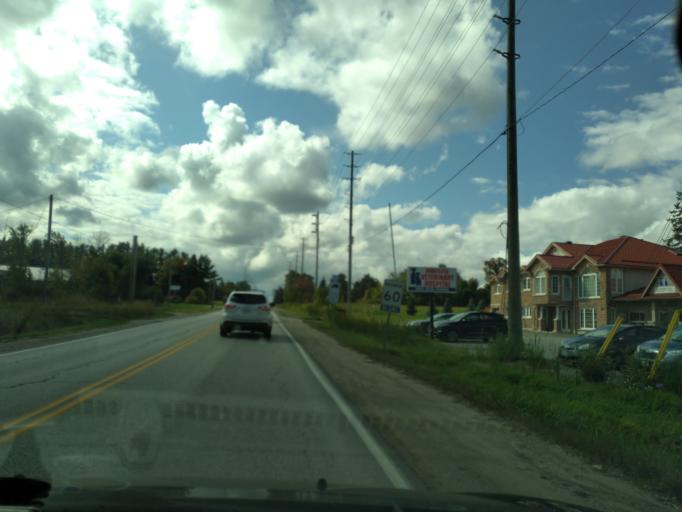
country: CA
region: Ontario
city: Innisfil
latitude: 44.3080
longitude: -79.5783
